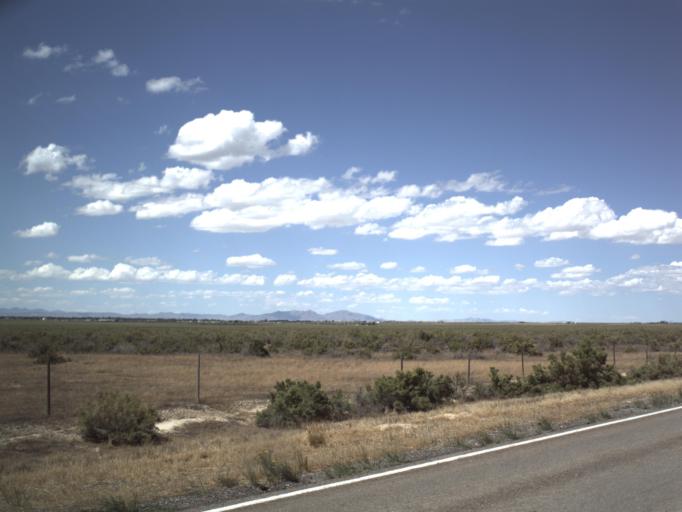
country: US
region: Utah
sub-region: Millard County
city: Delta
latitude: 39.3333
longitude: -112.4884
